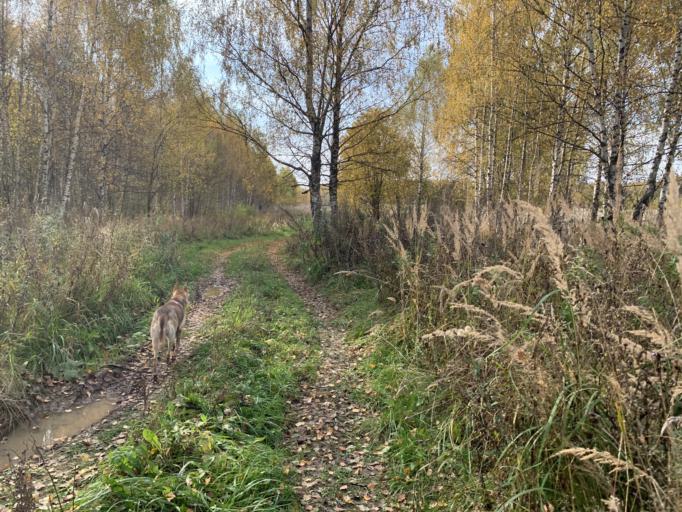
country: RU
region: Jaroslavl
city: Porech'ye-Rybnoye
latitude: 56.9907
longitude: 39.4062
